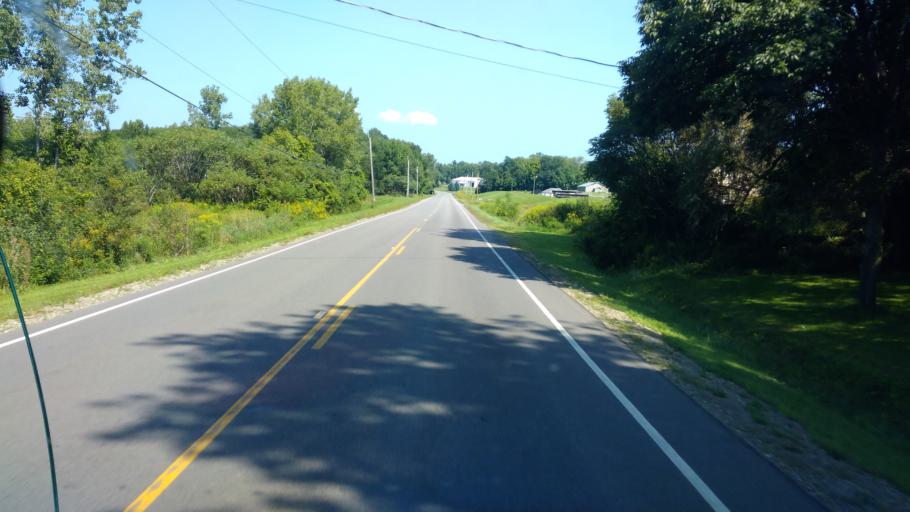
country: US
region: New York
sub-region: Allegany County
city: Belmont
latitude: 42.2563
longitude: -78.0389
